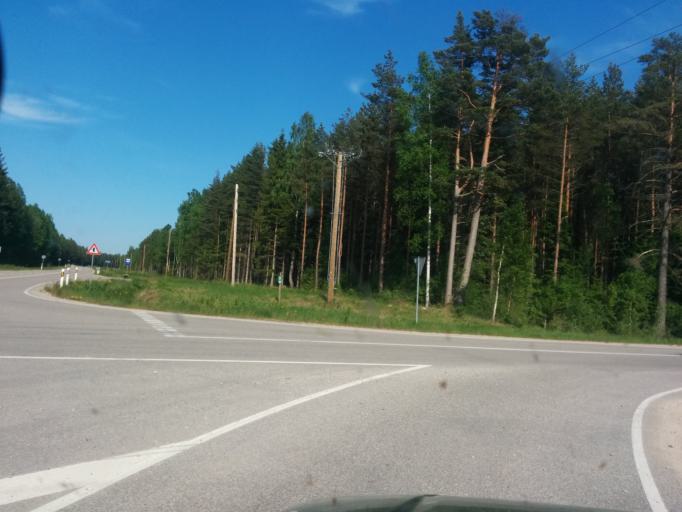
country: LV
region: Dundaga
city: Dundaga
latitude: 57.6739
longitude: 22.3234
